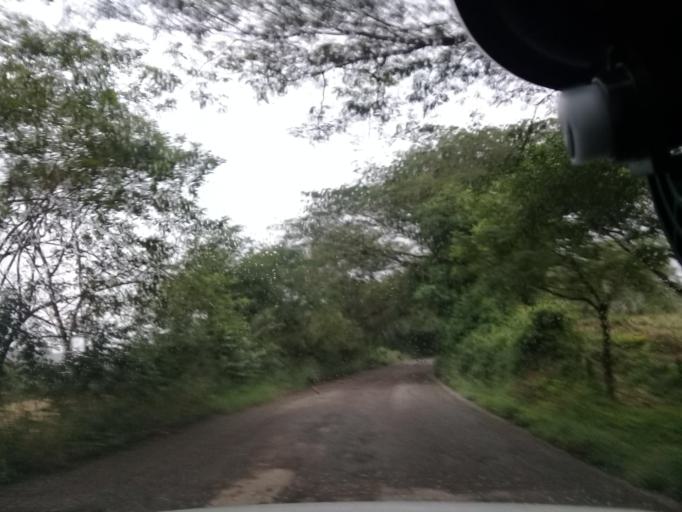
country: MX
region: Veracruz
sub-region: Chalma
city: San Pedro Coyutla
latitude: 21.2210
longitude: -98.3825
